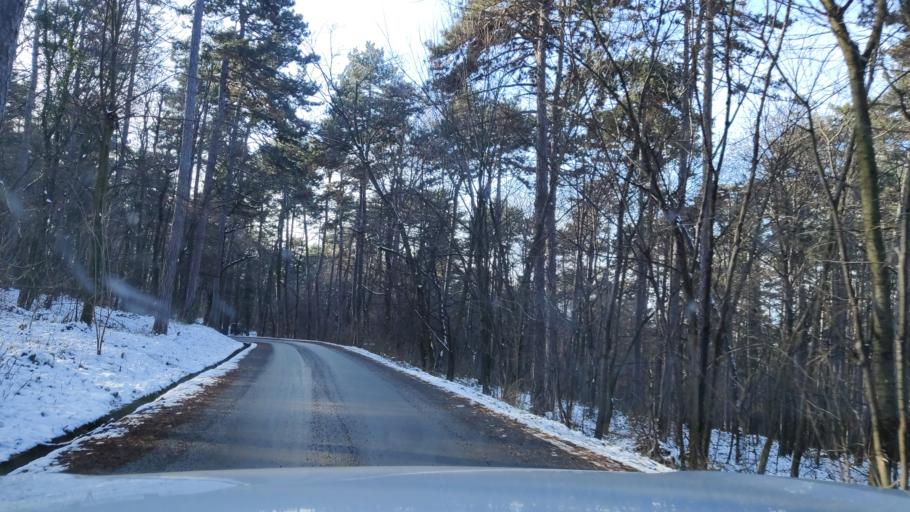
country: RS
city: Rusanj
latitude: 44.6994
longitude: 20.5106
